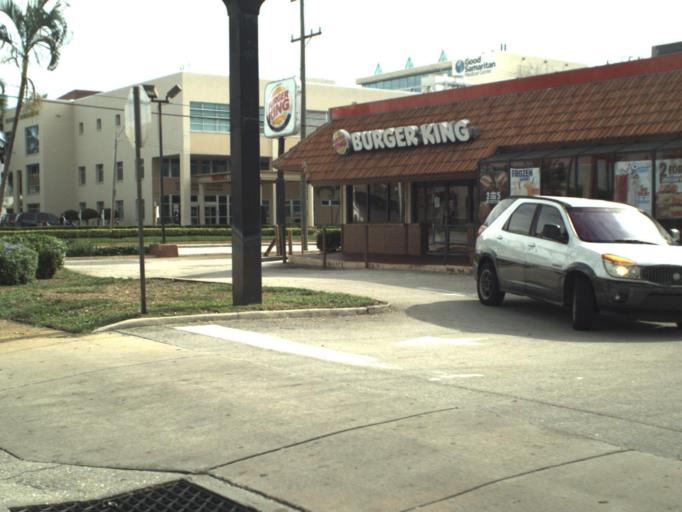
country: US
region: Florida
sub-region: Palm Beach County
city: West Palm Beach
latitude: 26.7240
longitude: -80.0532
